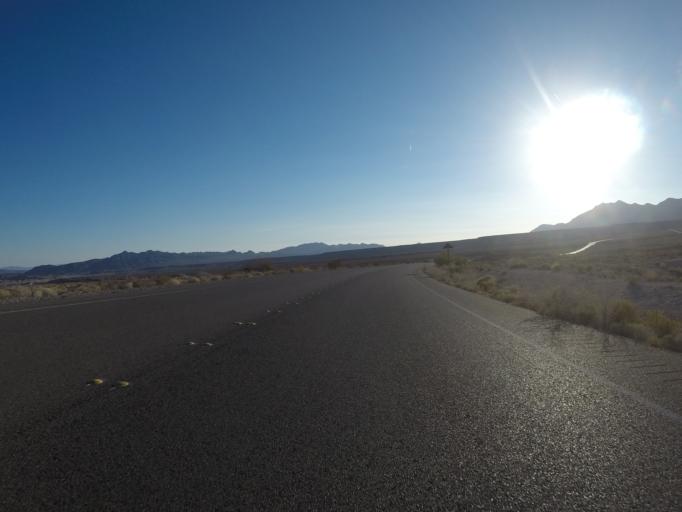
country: US
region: Nevada
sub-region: Clark County
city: Moapa Valley
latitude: 36.3710
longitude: -114.4439
